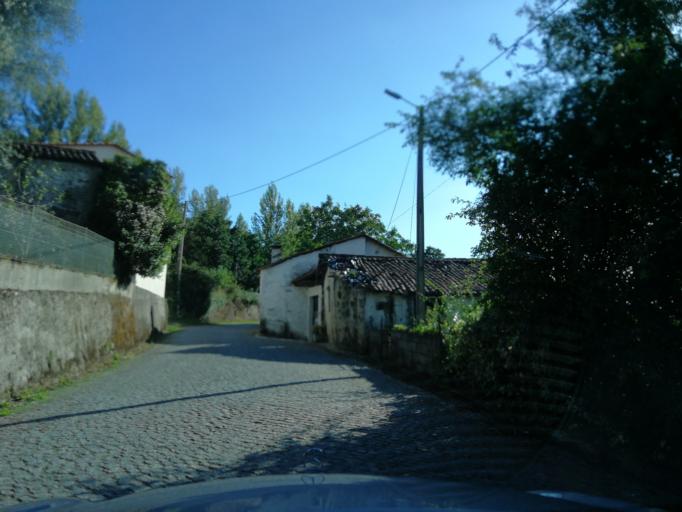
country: PT
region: Braga
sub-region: Braga
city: Adaufe
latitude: 41.5642
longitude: -8.3794
